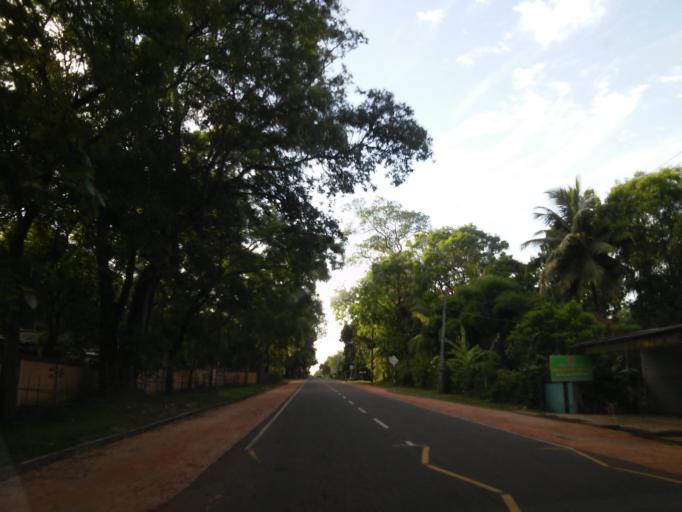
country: LK
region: North Central
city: Anuradhapura
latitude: 8.1268
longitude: 80.5637
